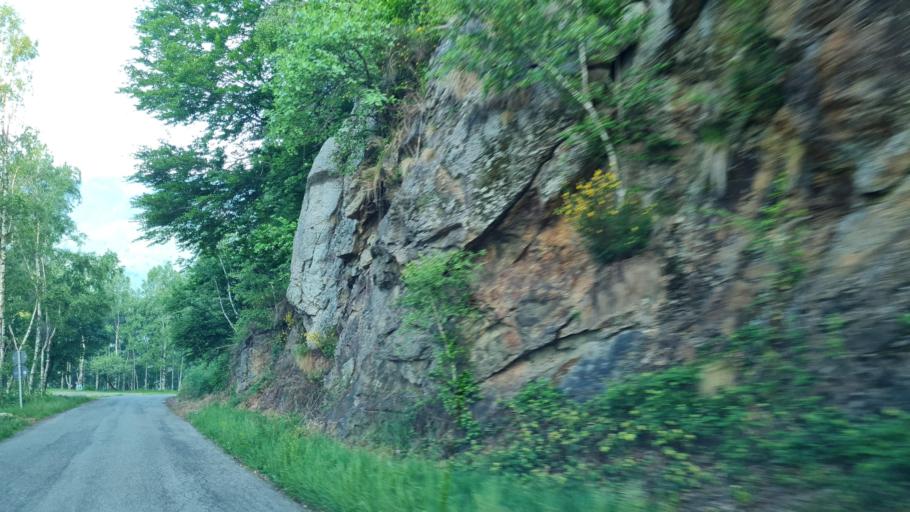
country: IT
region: Piedmont
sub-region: Provincia di Biella
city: Sordevolo
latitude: 45.5911
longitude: 7.9576
